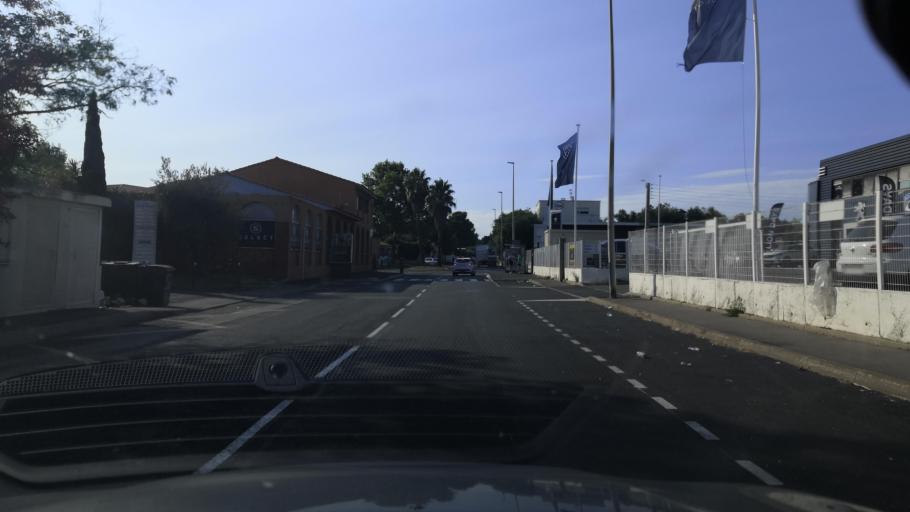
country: FR
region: Languedoc-Roussillon
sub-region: Departement de l'Herault
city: Lattes
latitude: 43.5818
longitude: 3.8805
